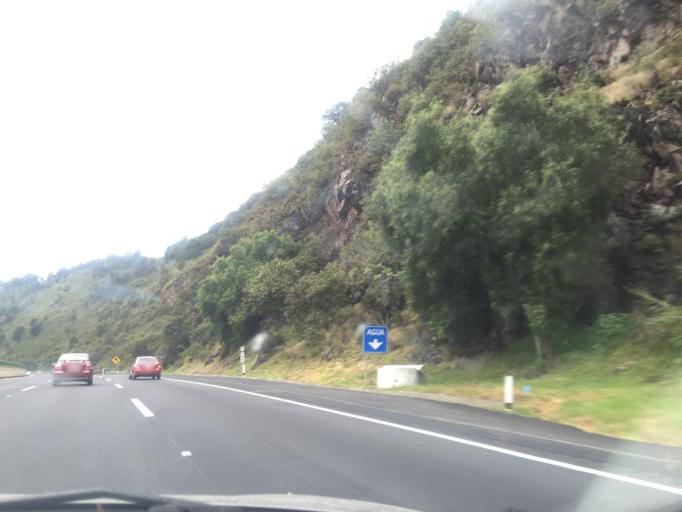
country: MX
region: Mexico City
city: Xochimilco
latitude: 19.2168
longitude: -99.1316
